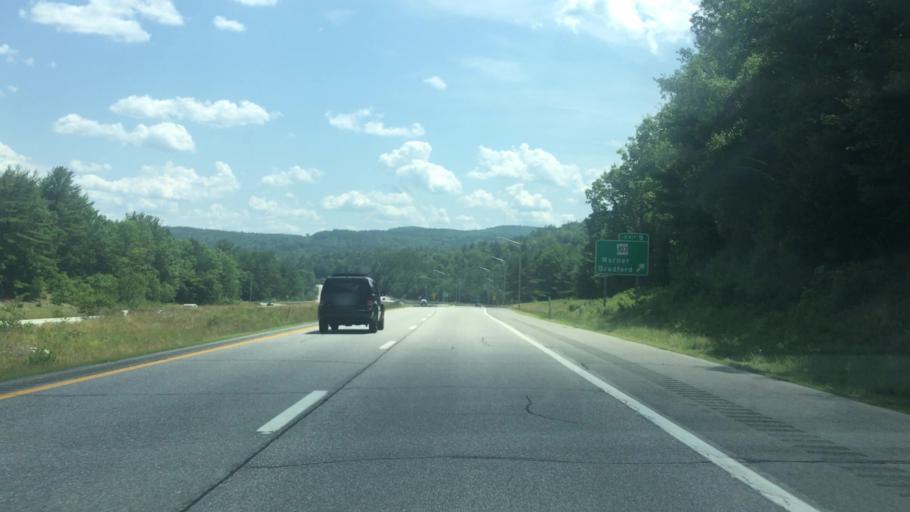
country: US
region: New Hampshire
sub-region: Merrimack County
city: Henniker
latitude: 43.2937
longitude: -71.8387
